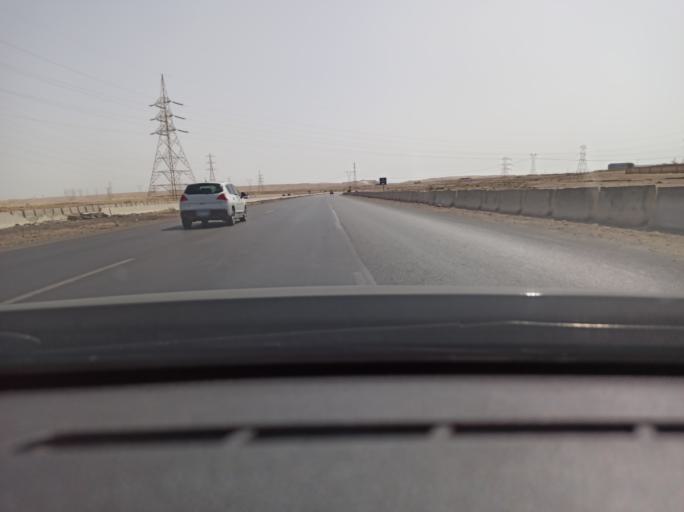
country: EG
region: Muhafazat al Qahirah
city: Halwan
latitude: 29.7665
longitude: 31.3930
